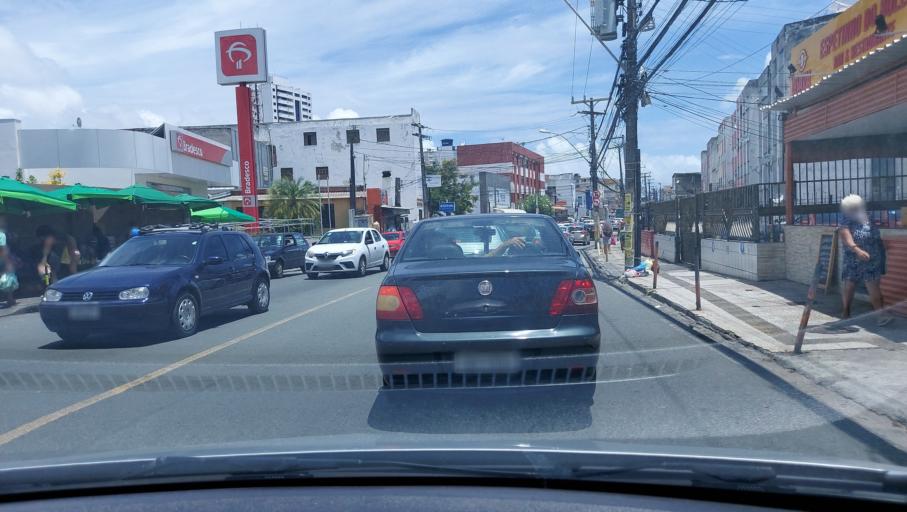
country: BR
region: Bahia
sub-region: Salvador
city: Salvador
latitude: -12.9887
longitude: -38.4816
